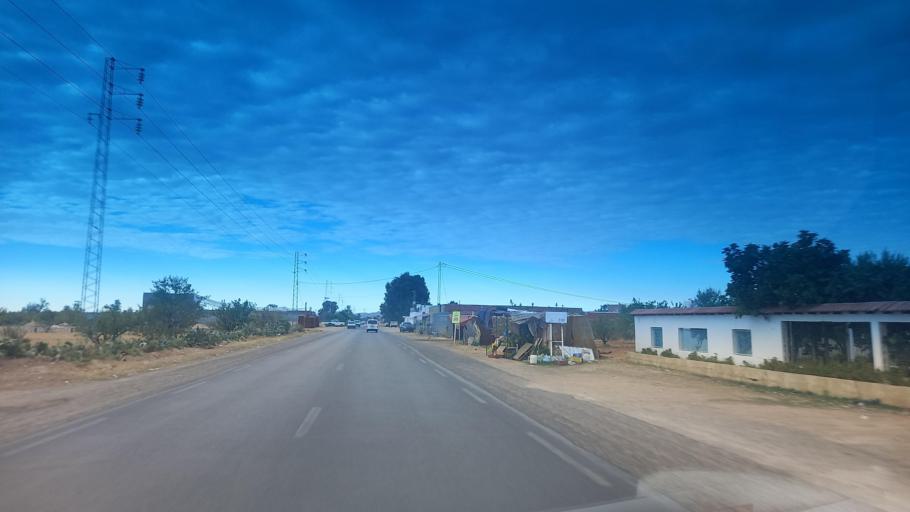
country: TN
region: Al Qasrayn
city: Kasserine
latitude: 35.2643
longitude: 9.0929
